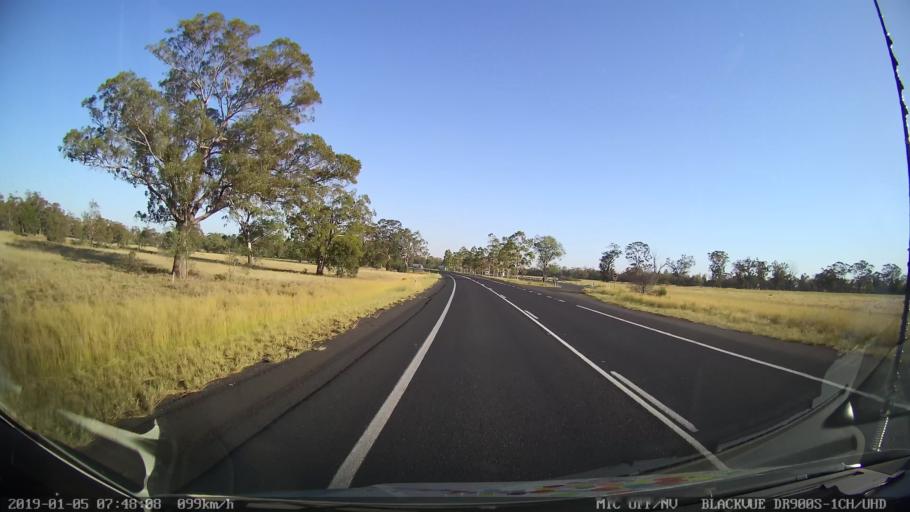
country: AU
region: New South Wales
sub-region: Gilgandra
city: Gilgandra
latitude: -31.8209
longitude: 148.6392
